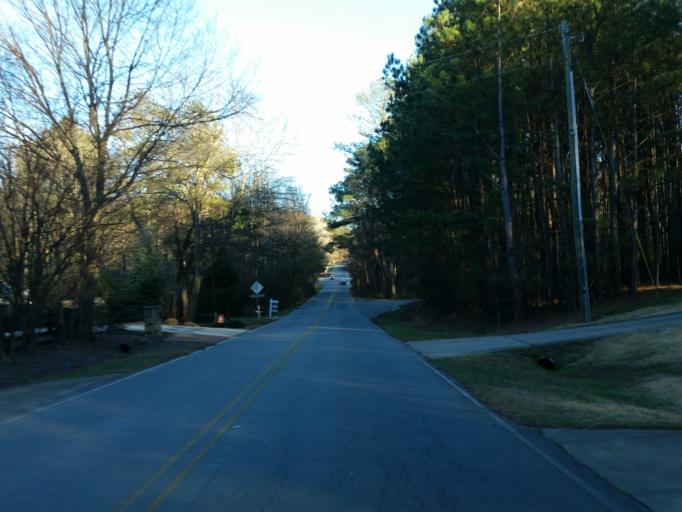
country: US
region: Georgia
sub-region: Cobb County
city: Marietta
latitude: 33.9639
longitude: -84.5997
